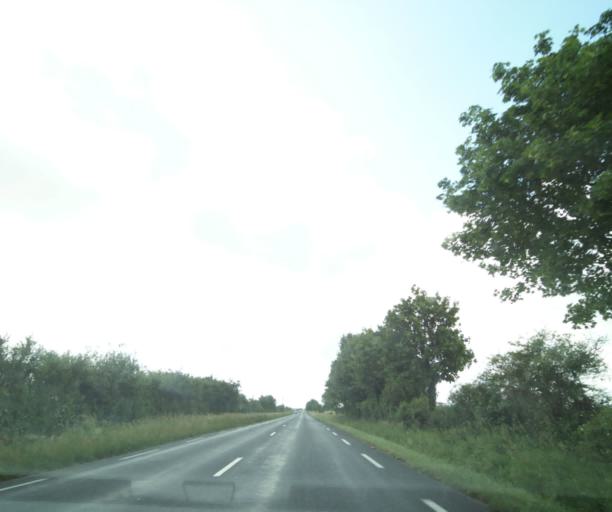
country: FR
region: Pays de la Loire
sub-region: Departement de la Sarthe
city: Vion
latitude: 47.8042
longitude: -0.2714
